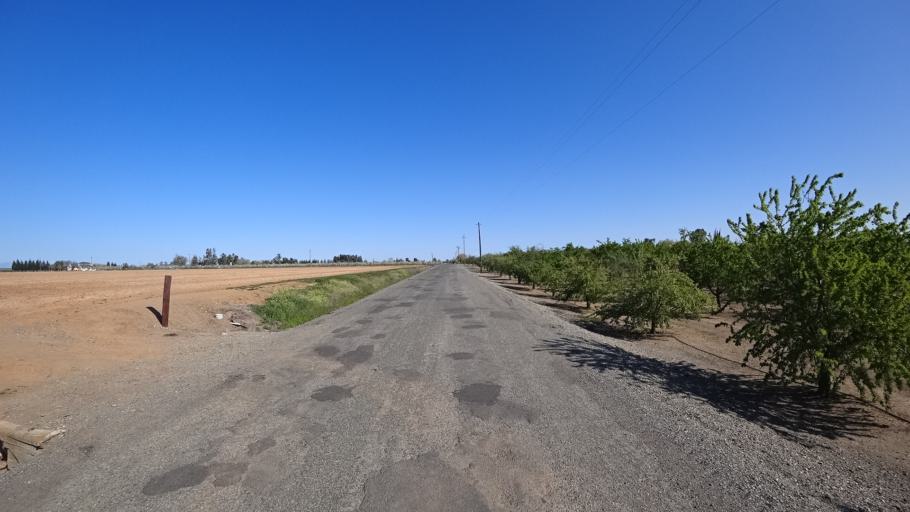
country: US
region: California
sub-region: Glenn County
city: Hamilton City
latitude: 39.7875
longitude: -122.0665
